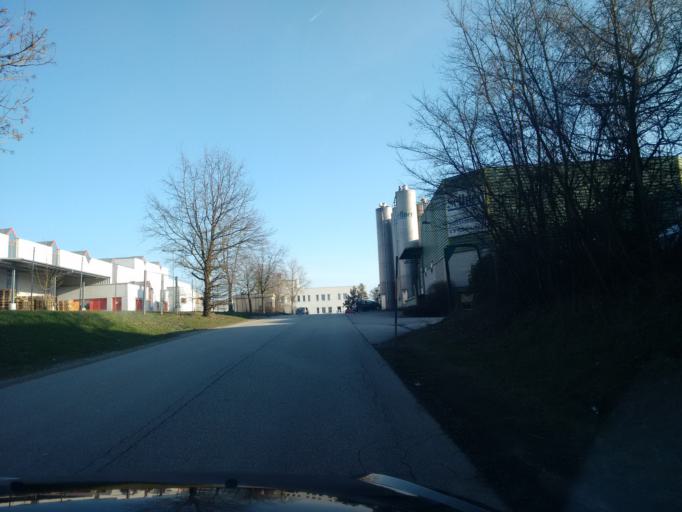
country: AT
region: Upper Austria
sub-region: Wels-Land
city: Holzhausen
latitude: 48.1891
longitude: 14.0786
